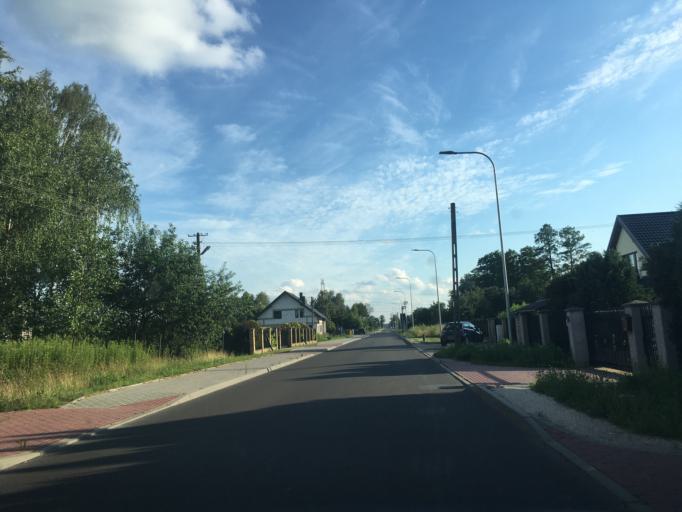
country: PL
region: Masovian Voivodeship
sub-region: Powiat wolominski
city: Radzymin
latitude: 52.4104
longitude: 21.2147
